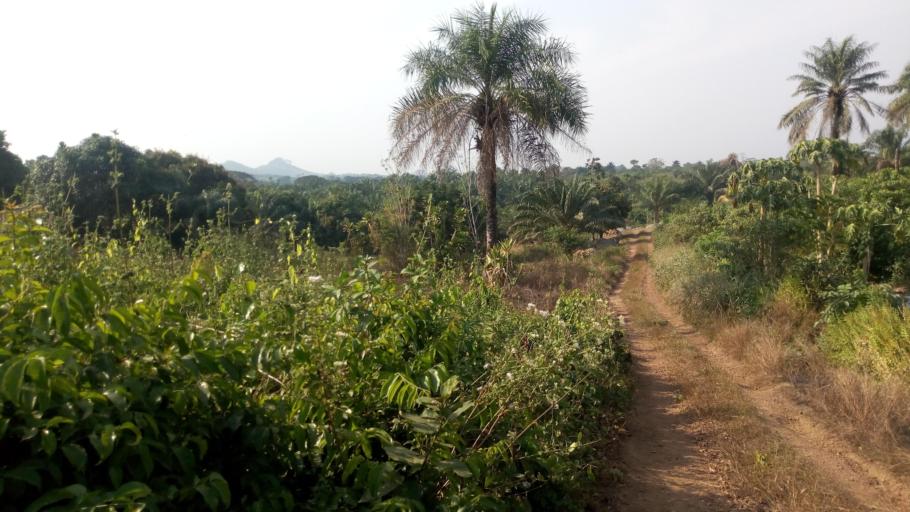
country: SL
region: Southern Province
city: Mogbwemo
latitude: 7.6155
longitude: -12.1823
